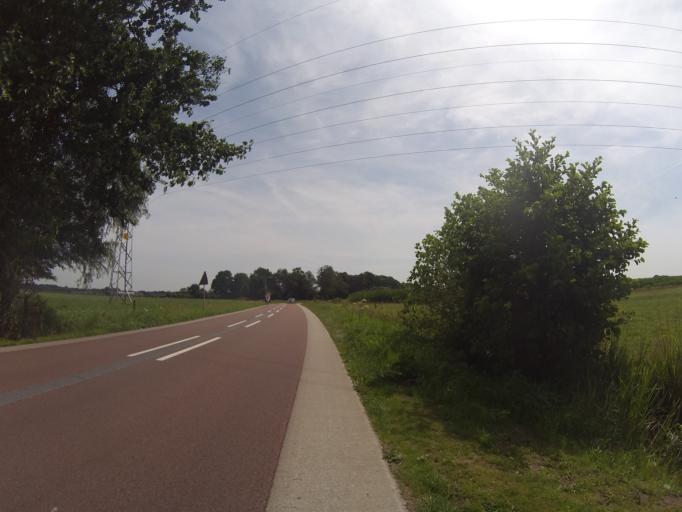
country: NL
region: Gelderland
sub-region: Gemeente Ermelo
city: Horst
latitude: 52.2639
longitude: 5.5503
